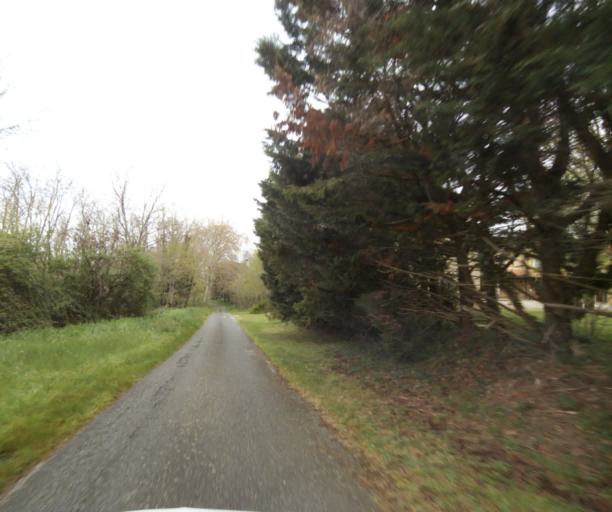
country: FR
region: Midi-Pyrenees
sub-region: Departement de l'Ariege
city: Saverdun
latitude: 43.2163
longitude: 1.5997
